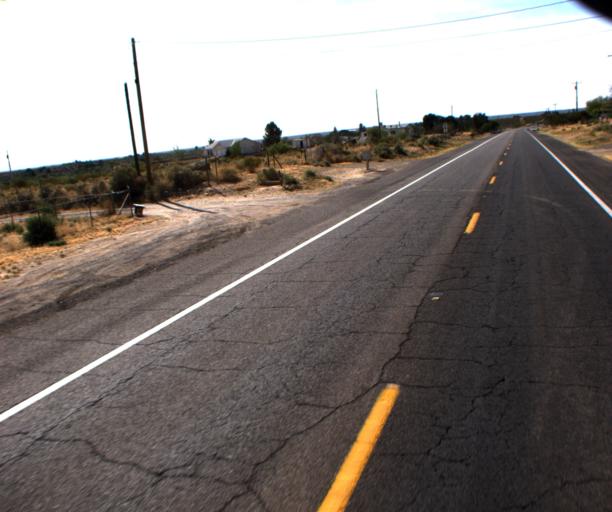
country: US
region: Arizona
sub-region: Graham County
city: Swift Trail Junction
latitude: 32.7240
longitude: -109.7116
